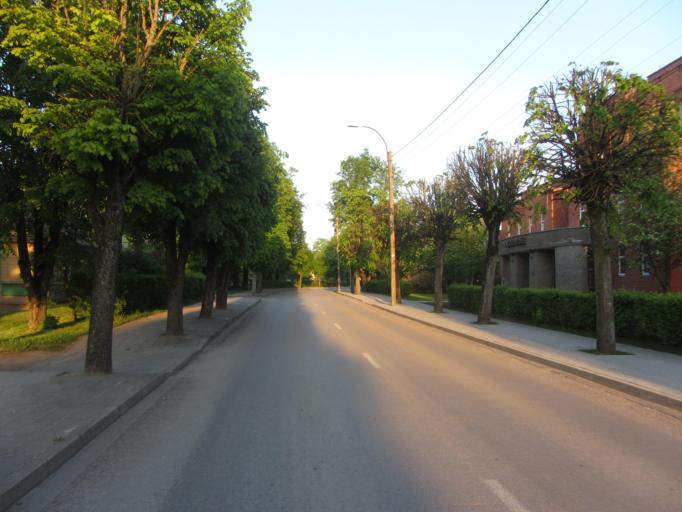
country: LT
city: Sirvintos
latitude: 55.0390
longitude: 24.9626
